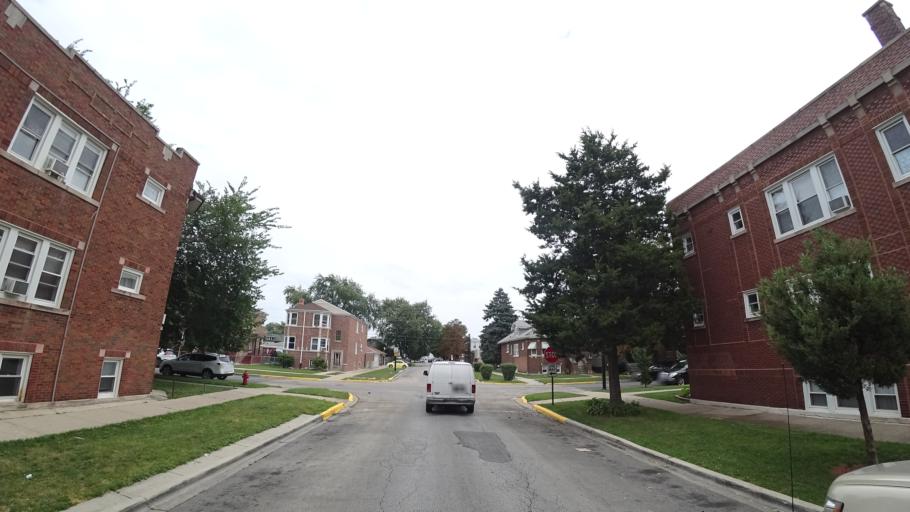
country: US
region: Illinois
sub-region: Cook County
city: Cicero
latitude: 41.8619
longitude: -87.7682
